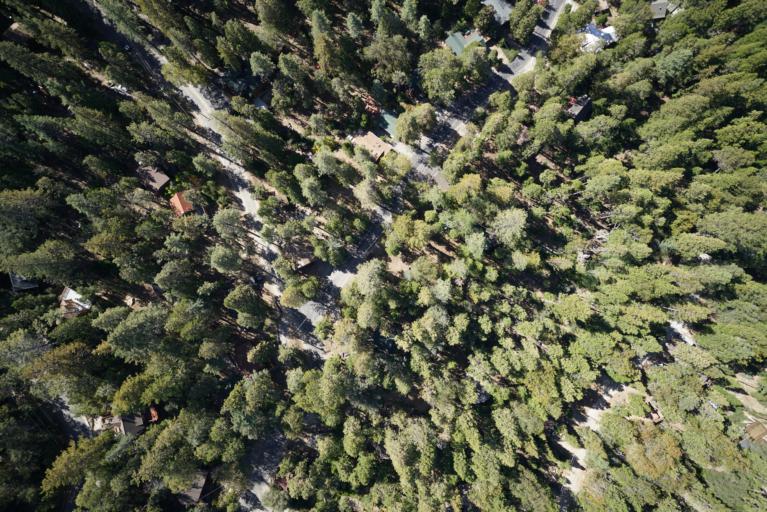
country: US
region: California
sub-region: Riverside County
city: Idyllwild
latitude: 33.7477
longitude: -116.6981
